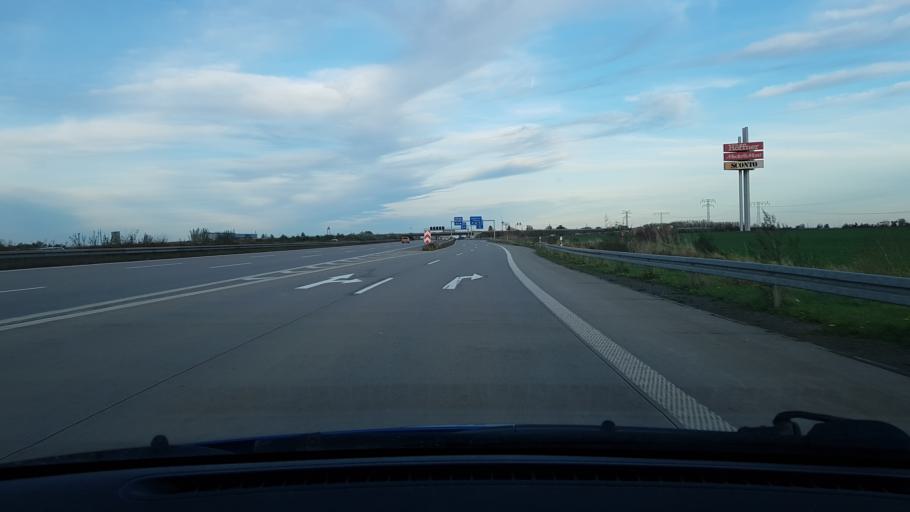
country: DE
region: Saxony-Anhalt
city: Barleben
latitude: 52.1837
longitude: 11.6092
